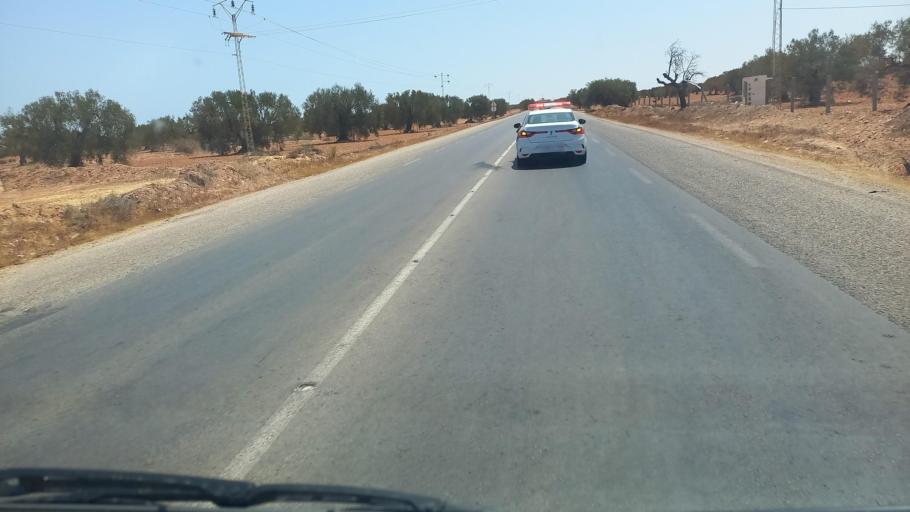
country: TN
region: Madanin
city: Zarzis
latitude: 33.5572
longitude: 11.0589
